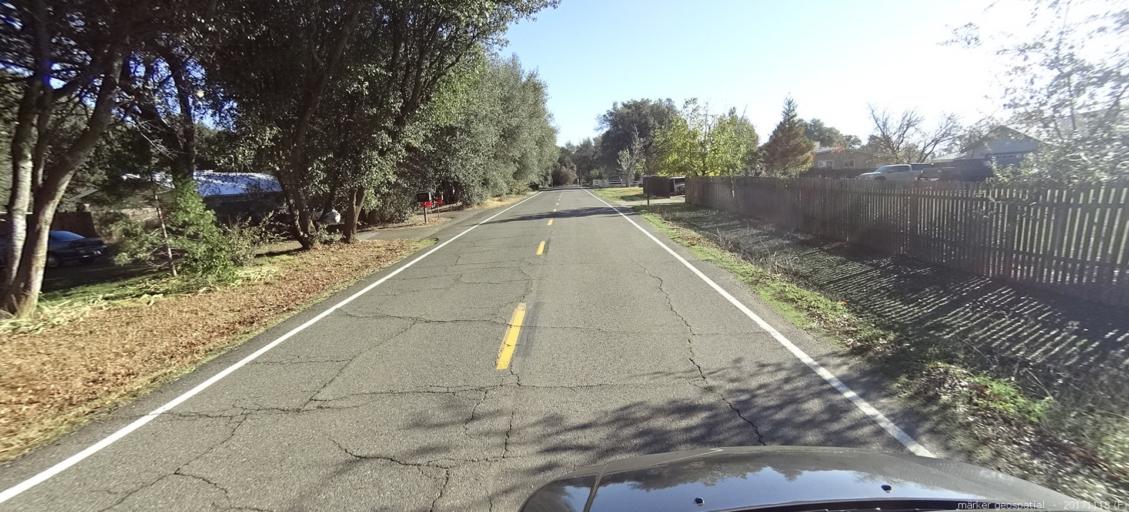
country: US
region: California
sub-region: Shasta County
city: Cottonwood
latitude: 40.3819
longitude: -122.3239
